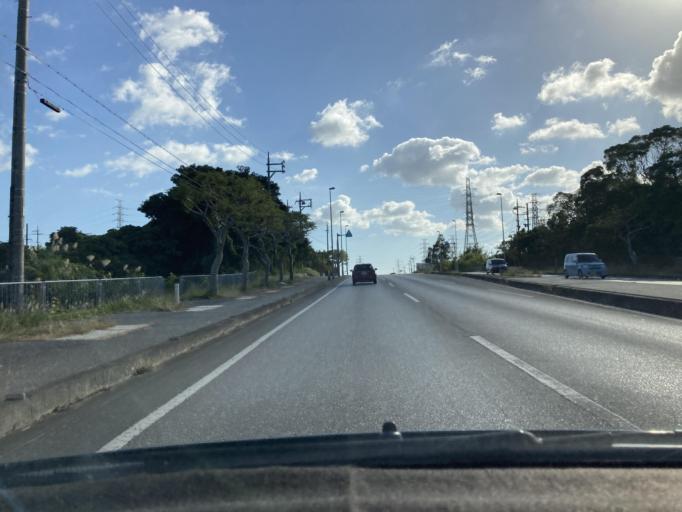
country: JP
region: Okinawa
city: Ishikawa
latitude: 26.3943
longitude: 127.8285
